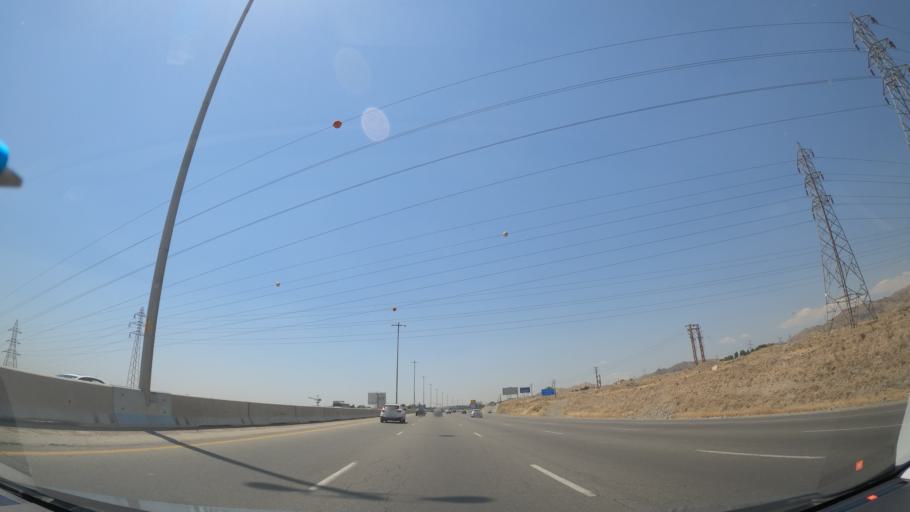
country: IR
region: Alborz
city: Karaj
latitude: 35.7716
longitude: 51.0446
